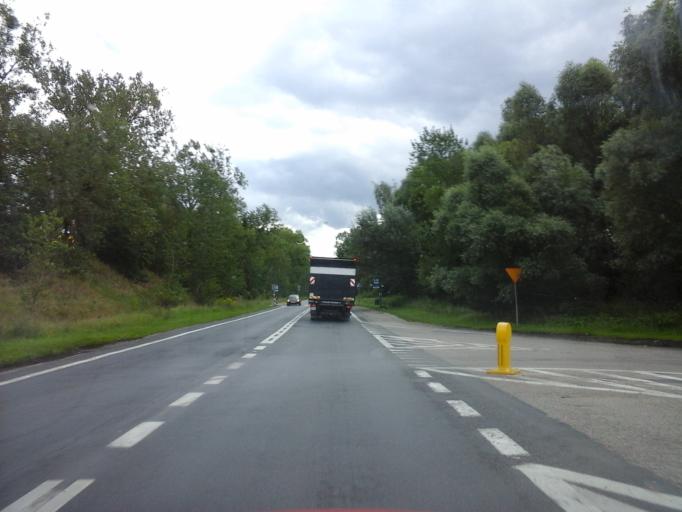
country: PL
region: West Pomeranian Voivodeship
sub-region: Szczecin
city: Szczecin
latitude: 53.3795
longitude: 14.5439
